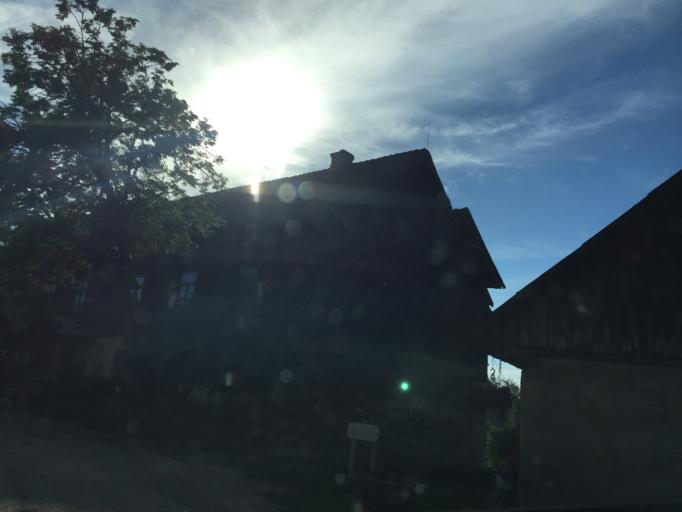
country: LV
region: Kuldigas Rajons
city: Kuldiga
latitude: 56.9914
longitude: 21.7631
